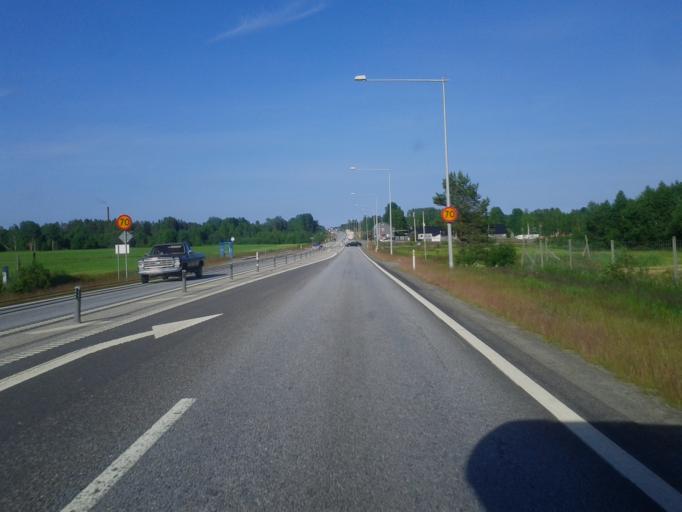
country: SE
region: Vaesterbotten
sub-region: Umea Kommun
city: Ersmark
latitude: 63.8539
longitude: 20.3770
